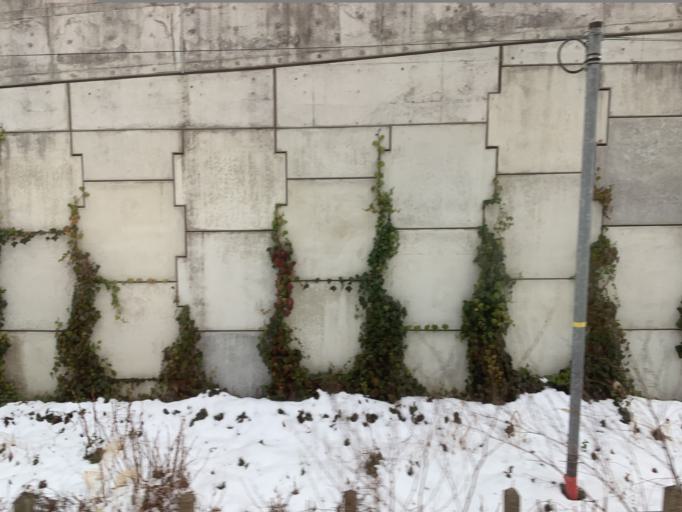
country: JP
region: Gifu
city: Takayama
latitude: 36.0205
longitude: 137.2910
